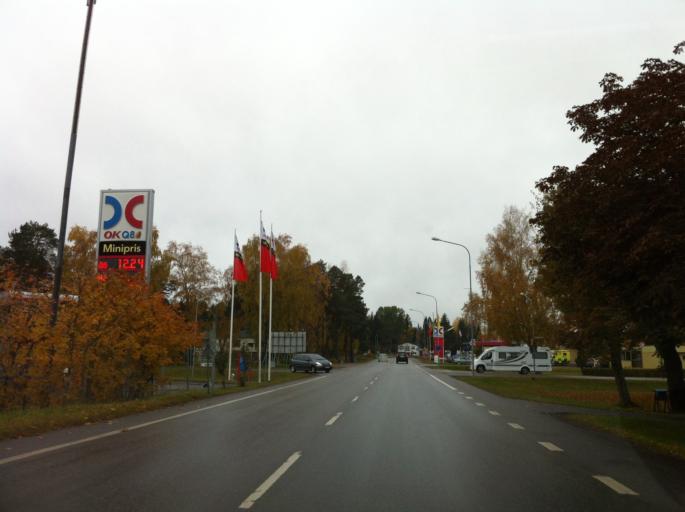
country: SE
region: Uppsala
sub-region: Osthammars Kommun
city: OEsthammar
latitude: 60.2566
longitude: 18.3500
